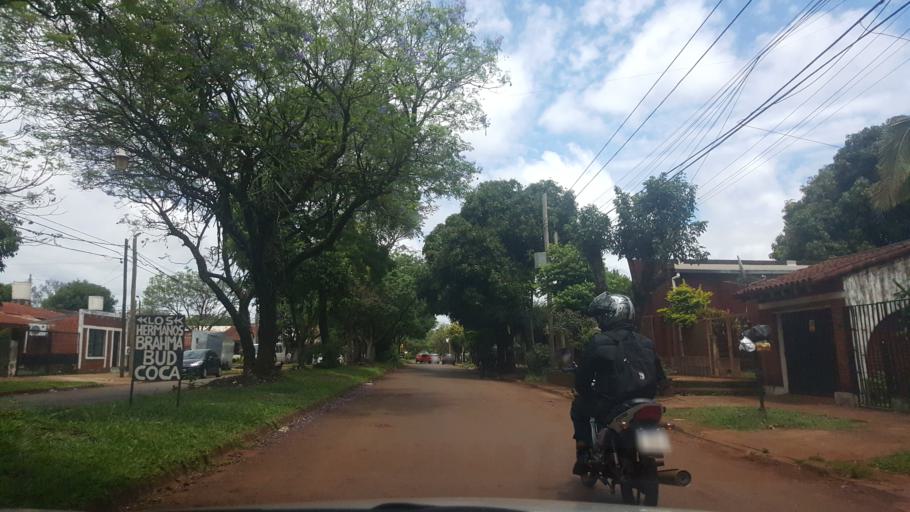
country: AR
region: Misiones
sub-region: Departamento de Capital
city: Posadas
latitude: -27.3735
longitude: -55.9251
